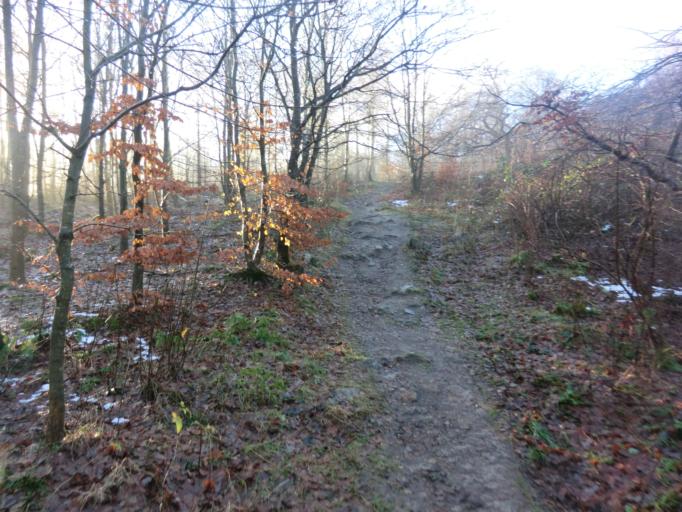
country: SE
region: Skane
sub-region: Lunds Kommun
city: Genarp
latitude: 55.6967
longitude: 13.3703
